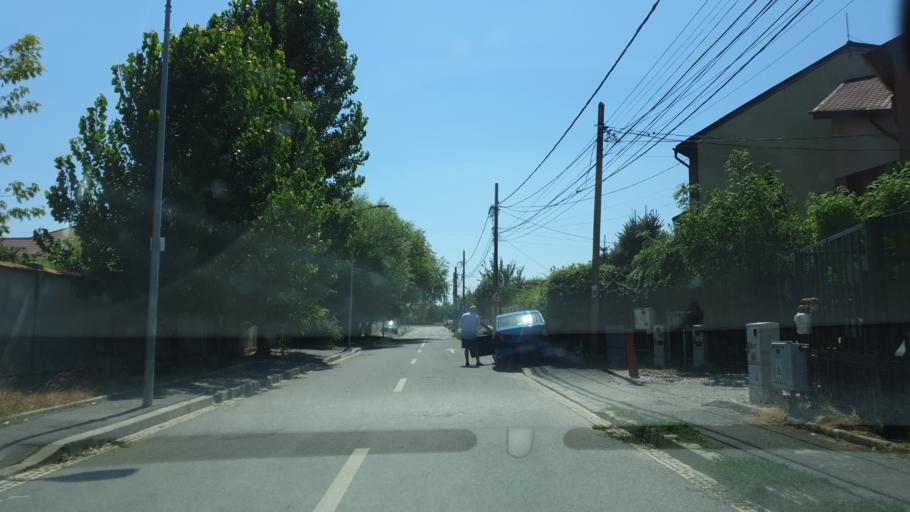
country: RO
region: Ilfov
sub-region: Comuna Chiajna
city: Rosu
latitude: 44.4655
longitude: 26.0213
